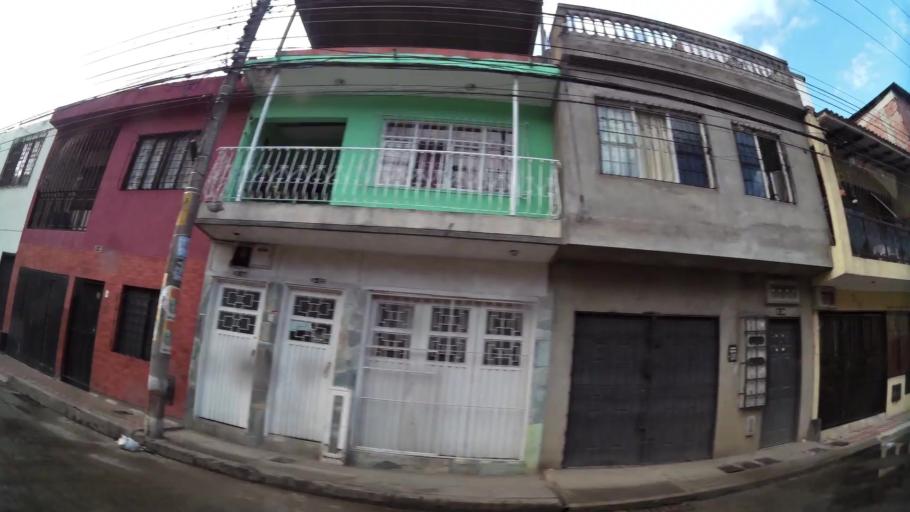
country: CO
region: Valle del Cauca
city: Cali
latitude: 3.4420
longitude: -76.5388
